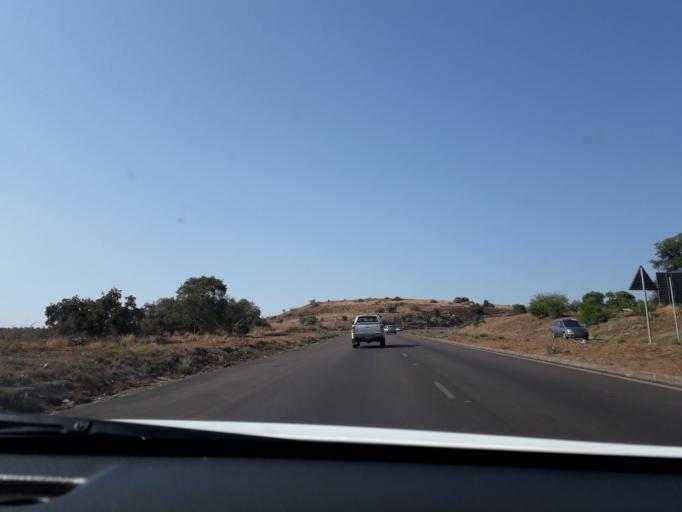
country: ZA
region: Gauteng
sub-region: City of Tshwane Metropolitan Municipality
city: Pretoria
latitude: -25.7831
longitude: 28.1923
